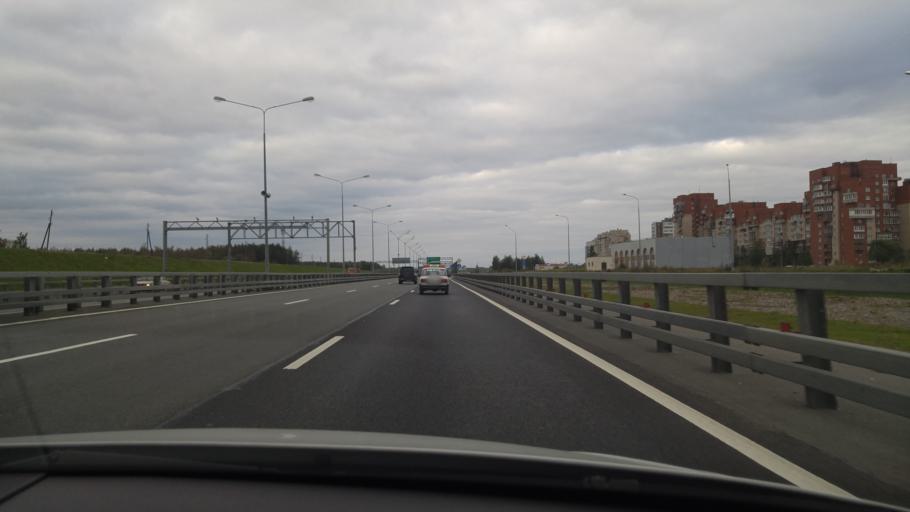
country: RU
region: St.-Petersburg
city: Kronshtadt
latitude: 60.0071
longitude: 29.7107
